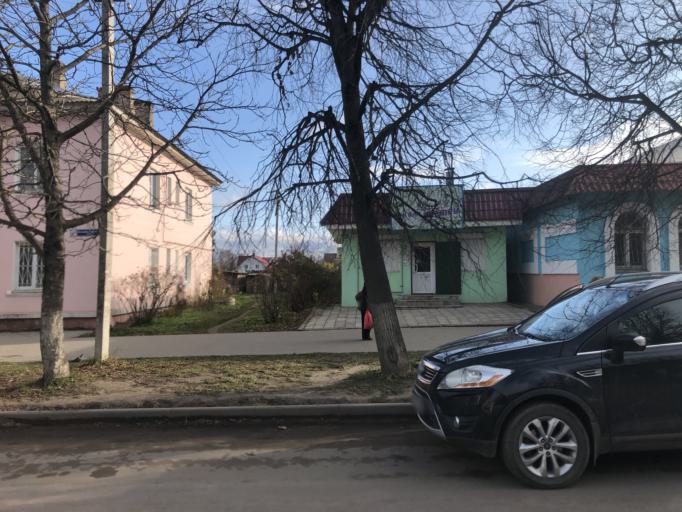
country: RU
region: Tverskaya
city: Rzhev
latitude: 56.2502
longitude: 34.3274
